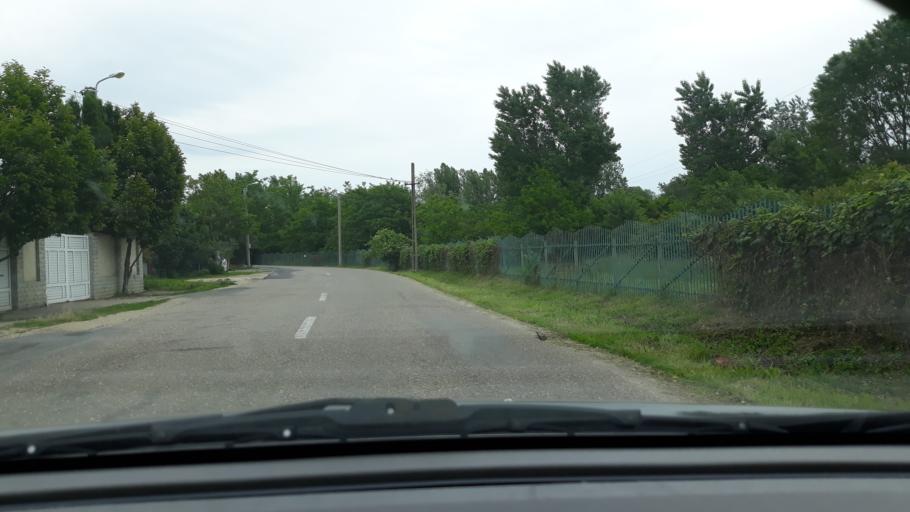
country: RO
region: Bihor
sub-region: Comuna Sanmartin
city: Sanmartin
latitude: 47.0527
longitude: 21.9994
